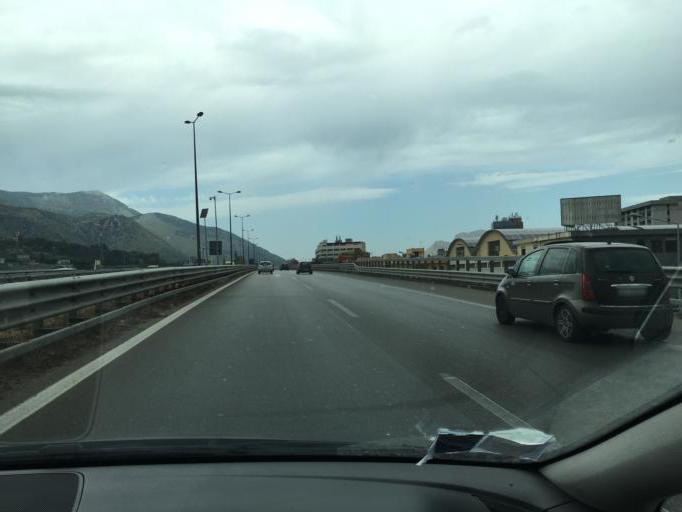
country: IT
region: Sicily
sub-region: Palermo
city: Palermo
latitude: 38.1552
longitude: 13.3184
